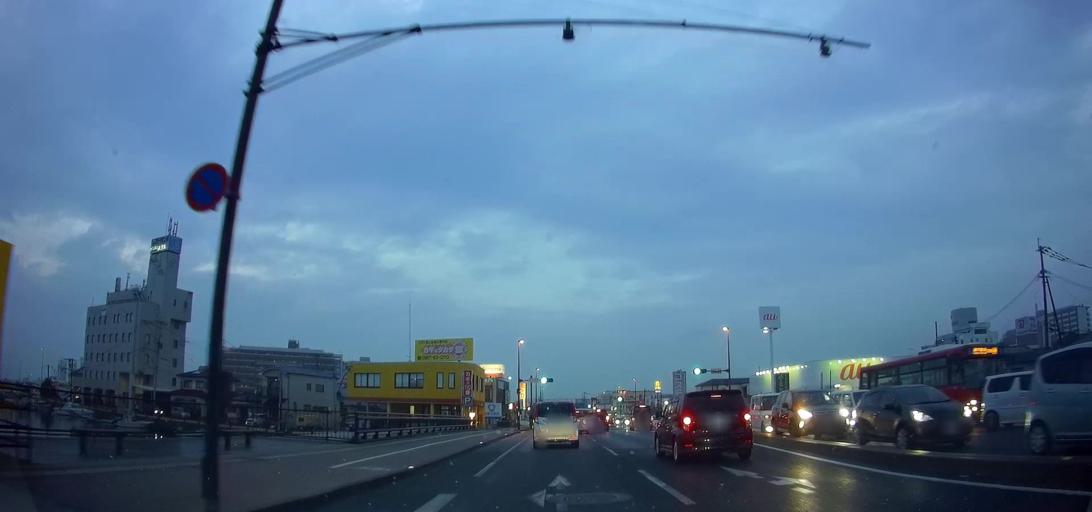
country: JP
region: Nagasaki
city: Omura
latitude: 32.9037
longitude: 129.9578
